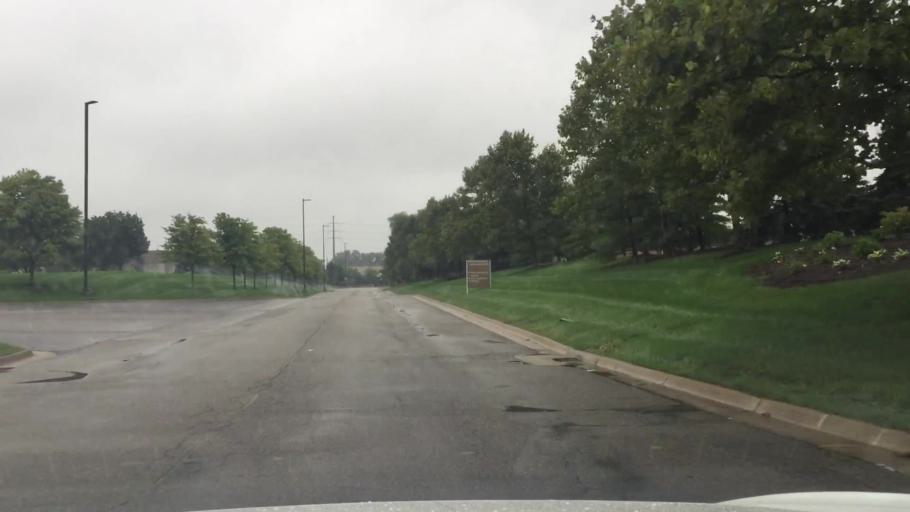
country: US
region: Michigan
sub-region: Wayne County
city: Livonia
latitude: 42.3802
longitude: -83.3267
